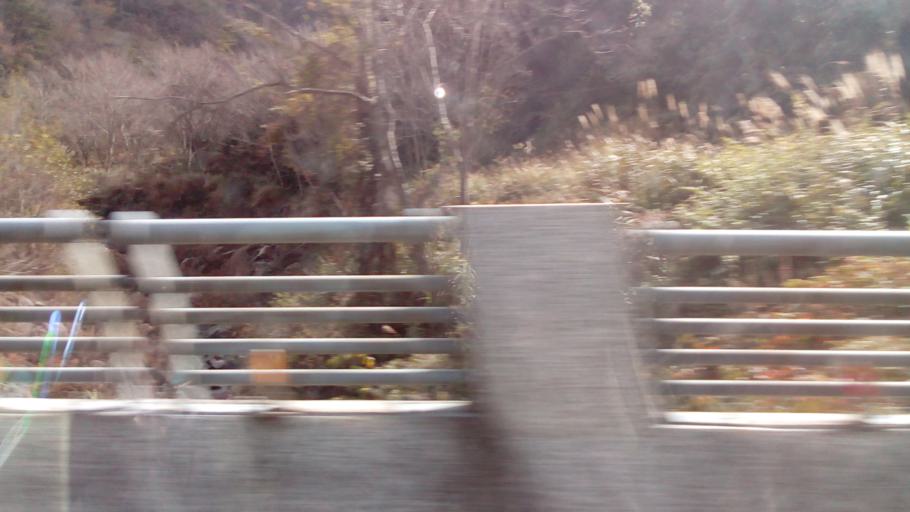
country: TW
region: Taiwan
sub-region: Hualien
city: Hualian
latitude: 24.3660
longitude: 121.3375
